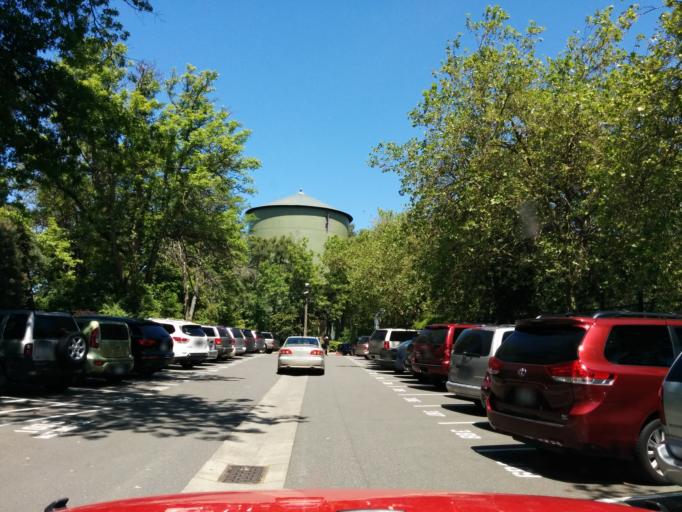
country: US
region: Washington
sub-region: King County
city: Seattle
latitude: 47.6666
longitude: -122.3540
